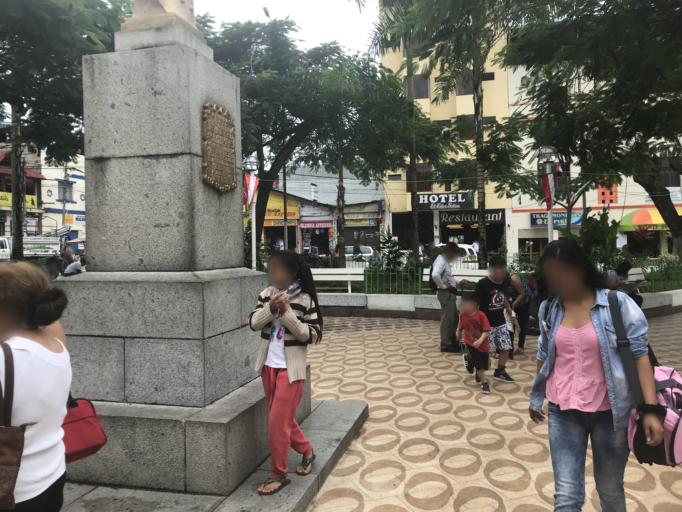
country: PE
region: Junin
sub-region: Chanchamayo
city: La Merced
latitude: -11.0561
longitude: -75.3283
